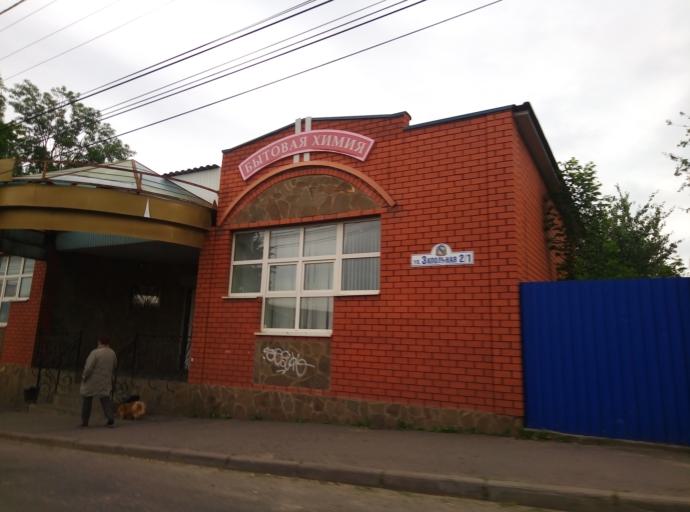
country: RU
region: Kursk
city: Kursk
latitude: 51.7446
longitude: 36.1632
